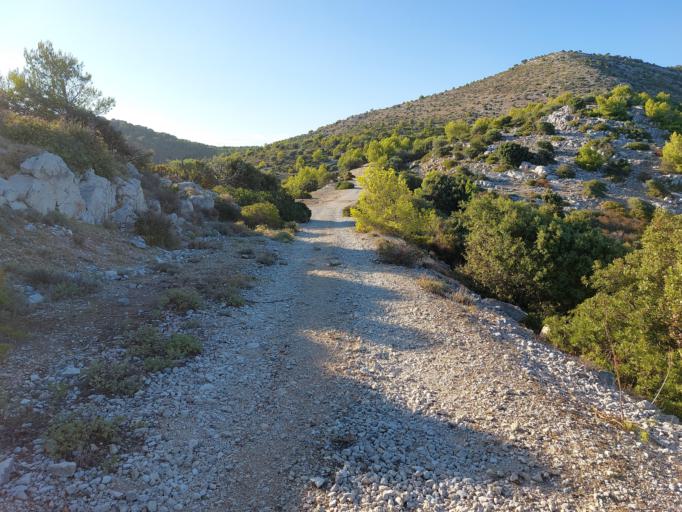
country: HR
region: Dubrovacko-Neretvanska
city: Smokvica
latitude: 42.7294
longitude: 16.8414
